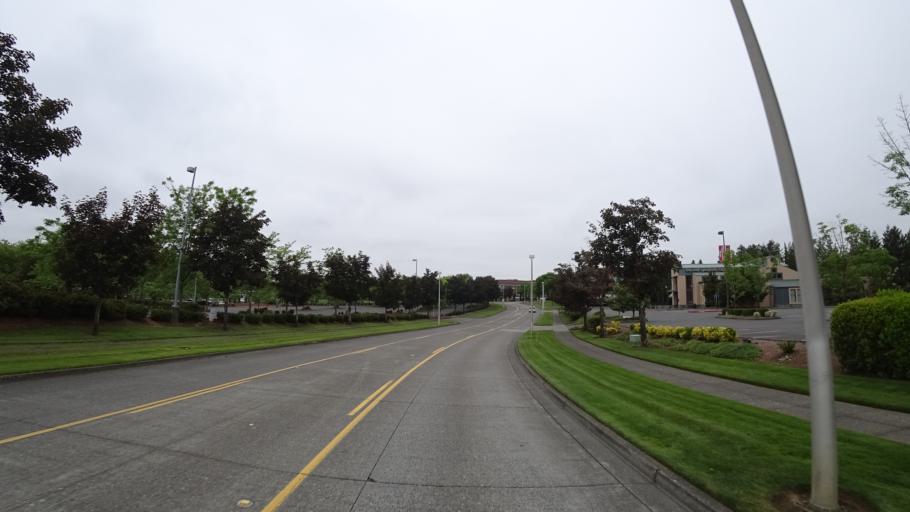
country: US
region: Oregon
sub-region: Washington County
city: Rockcreek
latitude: 45.5400
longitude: -122.8719
